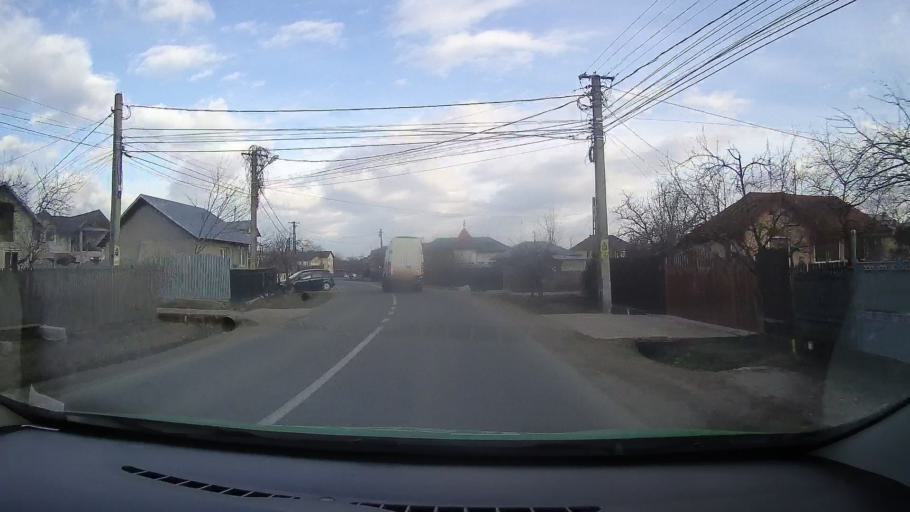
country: RO
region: Dambovita
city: Razvad
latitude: 44.9331
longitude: 25.5438
